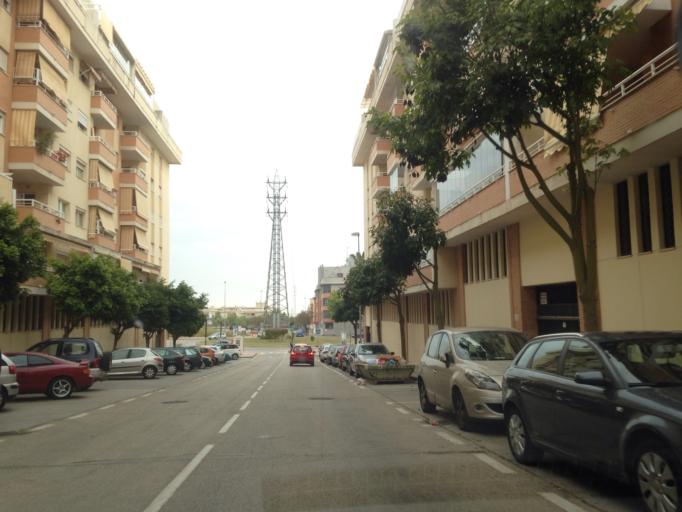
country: ES
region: Andalusia
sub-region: Provincia de Malaga
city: Malaga
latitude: 36.7253
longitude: -4.4746
